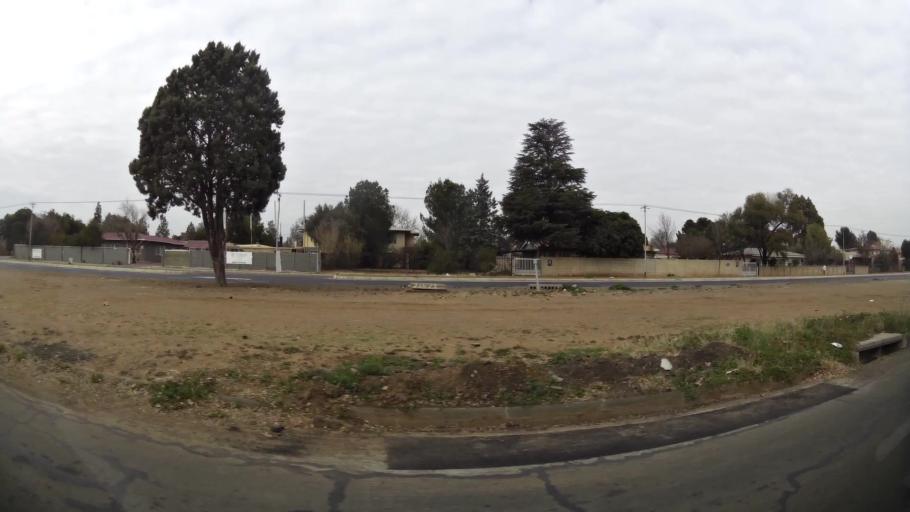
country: ZA
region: Orange Free State
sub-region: Mangaung Metropolitan Municipality
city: Bloemfontein
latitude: -29.1256
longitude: 26.1892
